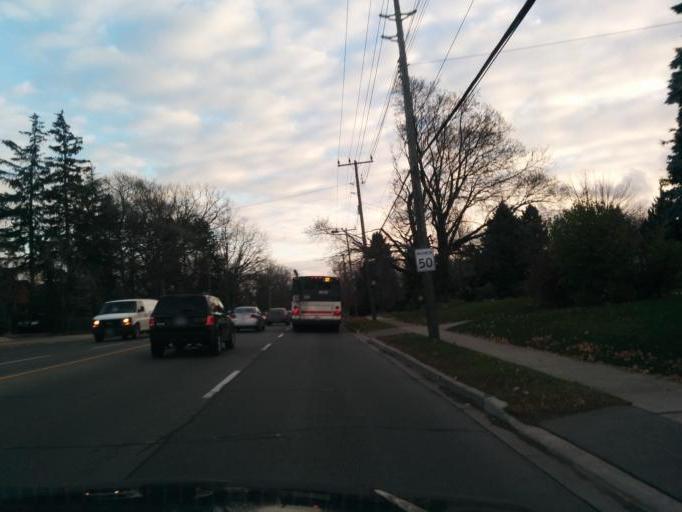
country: CA
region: Ontario
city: Etobicoke
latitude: 43.6679
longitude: -79.5338
